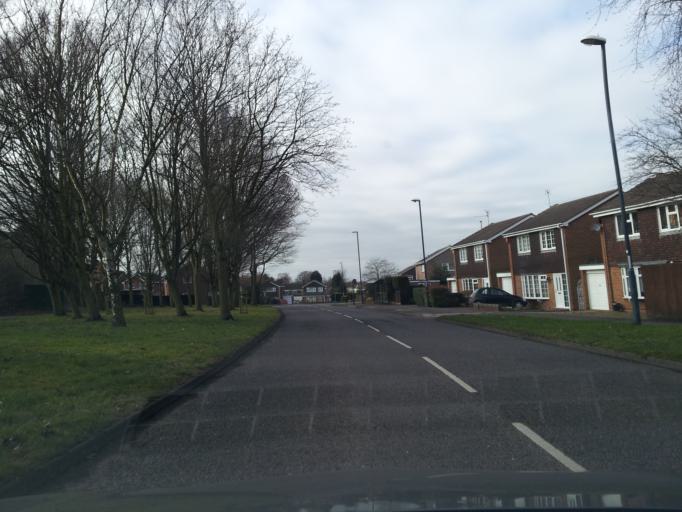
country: GB
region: England
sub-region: Derbyshire
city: Findern
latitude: 52.9136
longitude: -1.5435
